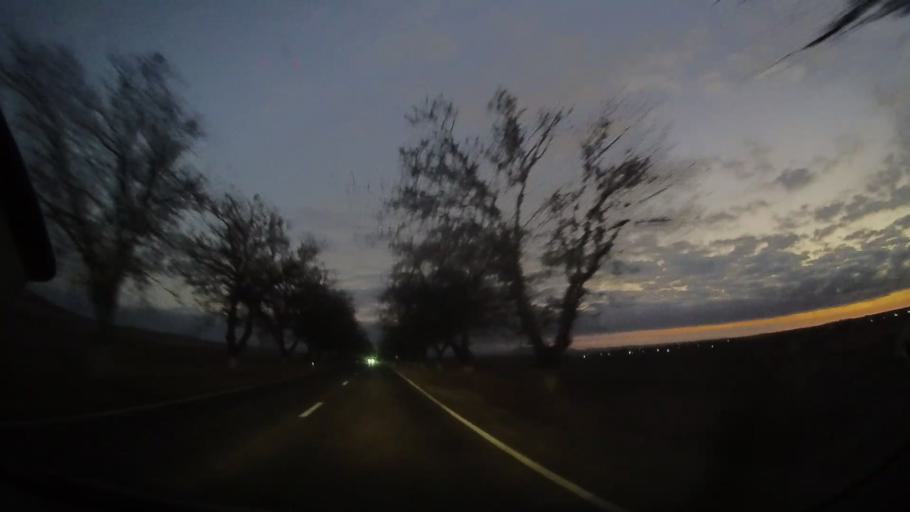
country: RO
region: Tulcea
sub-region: Comuna Frecatei
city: Cataloi
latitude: 45.0983
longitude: 28.7420
